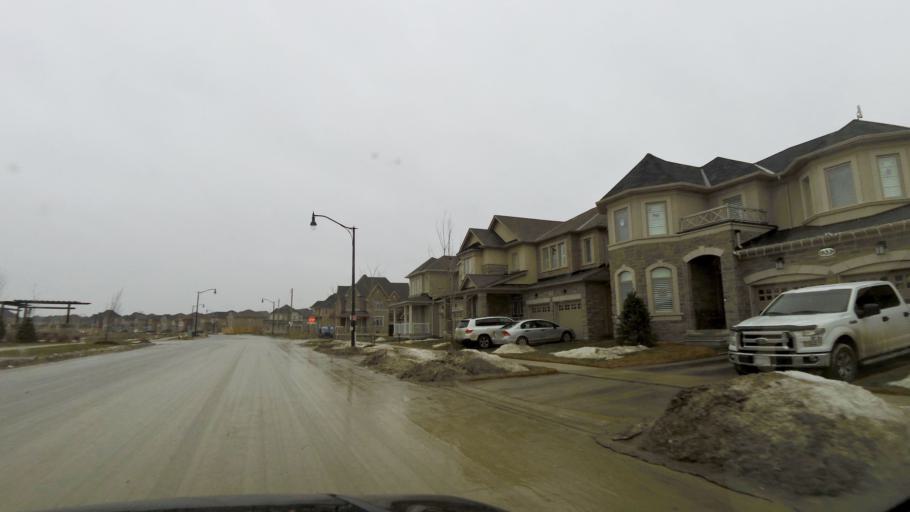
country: CA
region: Ontario
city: Brampton
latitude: 43.8121
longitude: -79.7267
